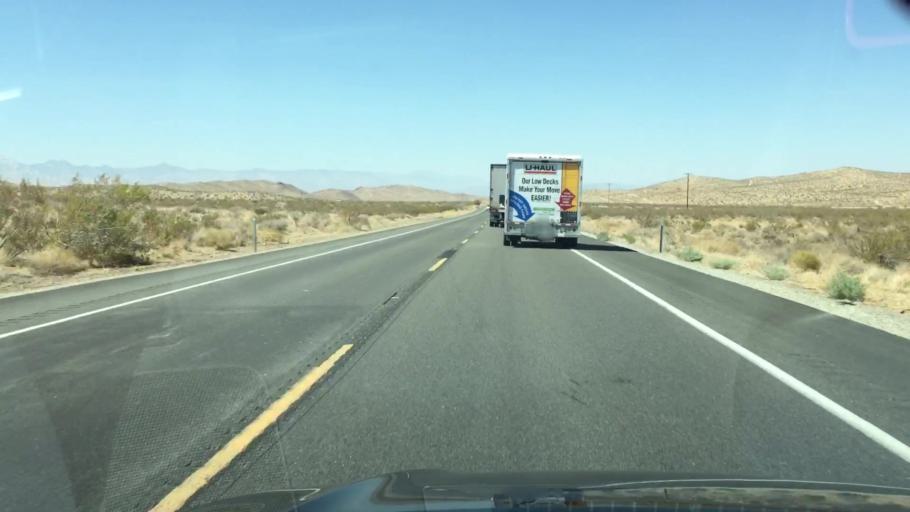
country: US
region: California
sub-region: Kern County
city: Ridgecrest
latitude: 35.5113
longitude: -117.6692
